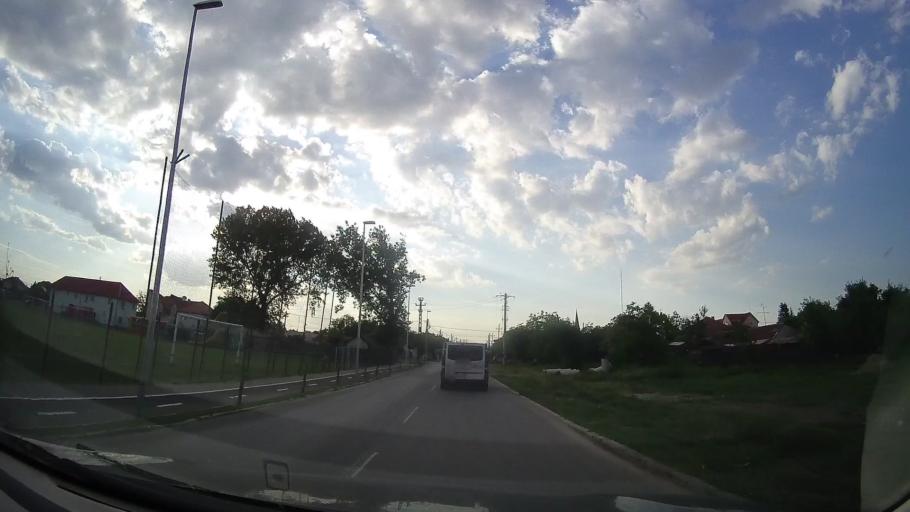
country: RO
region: Timis
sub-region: Comuna Dumbravita
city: Dumbravita
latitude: 45.7993
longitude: 21.2519
